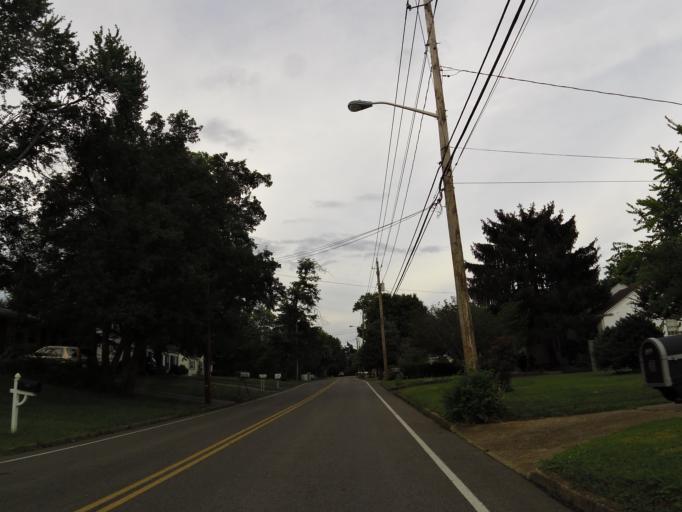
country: US
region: Tennessee
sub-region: Knox County
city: Knoxville
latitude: 36.0121
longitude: -83.9107
